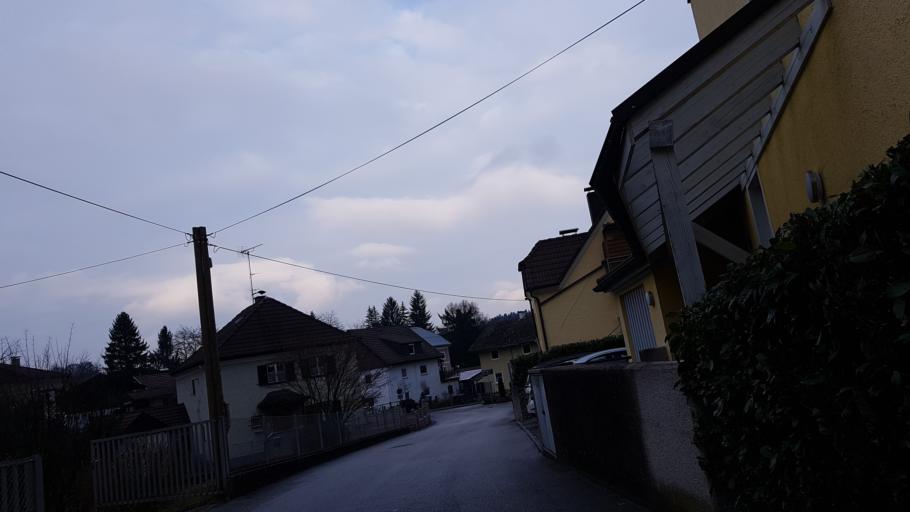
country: AT
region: Salzburg
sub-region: Politischer Bezirk Salzburg-Umgebung
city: Oberndorf bei Salzburg
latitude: 47.9447
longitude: 12.9351
